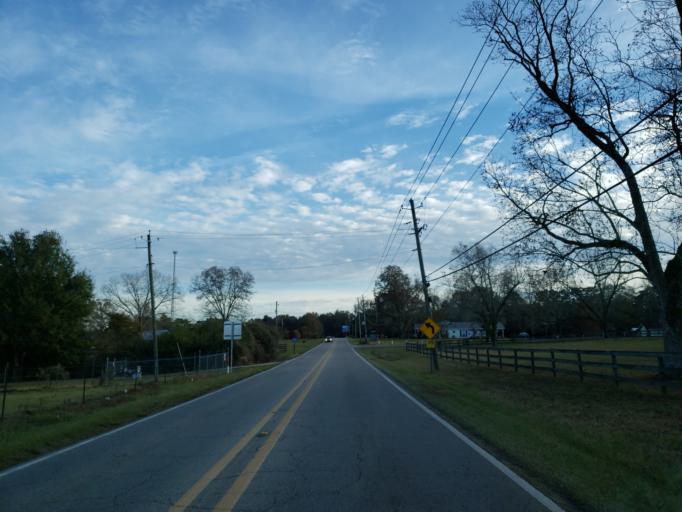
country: US
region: Mississippi
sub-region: Lamar County
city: Purvis
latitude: 31.1597
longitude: -89.4209
